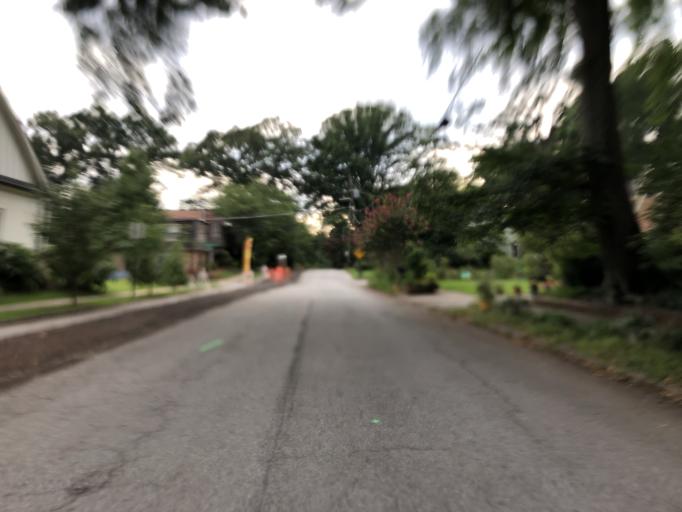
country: US
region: Georgia
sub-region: DeKalb County
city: Decatur
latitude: 33.7784
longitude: -84.3018
